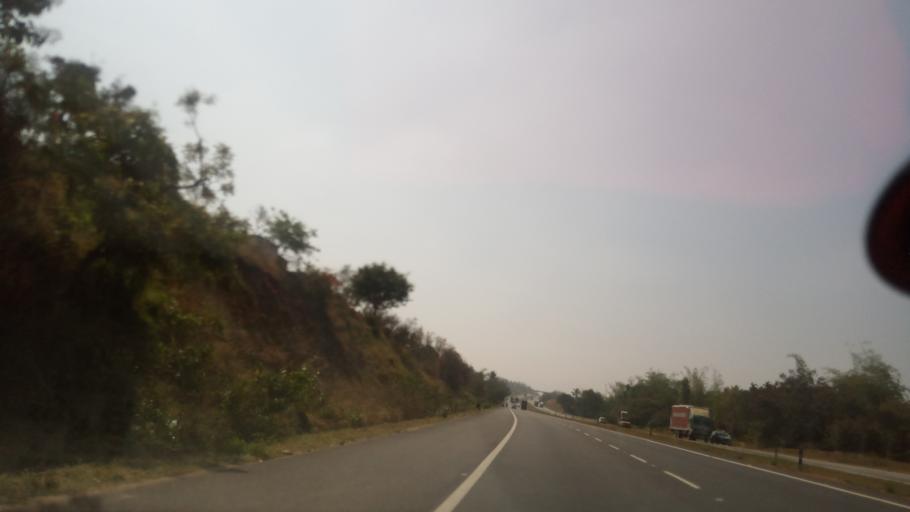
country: IN
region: Karnataka
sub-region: Bangalore Urban
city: Bangalore
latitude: 12.9825
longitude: 77.4708
